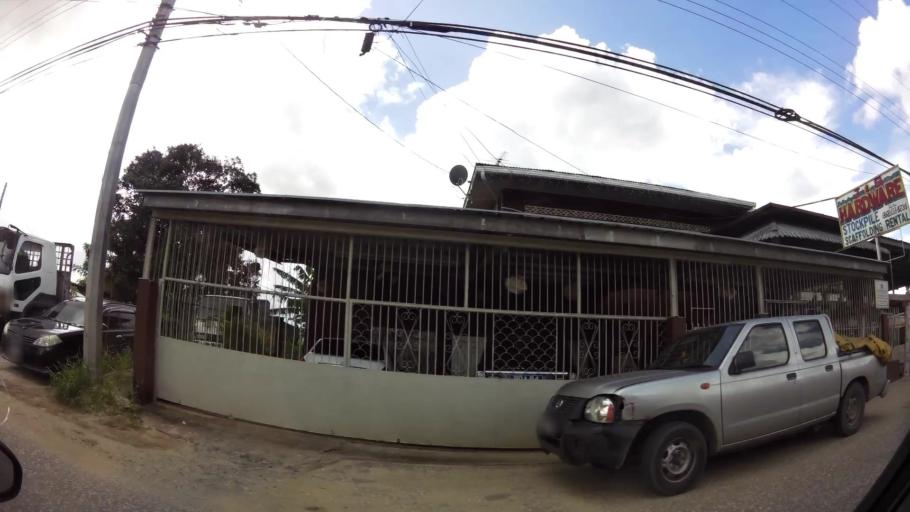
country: TT
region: Penal/Debe
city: Debe
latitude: 10.2299
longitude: -61.4410
